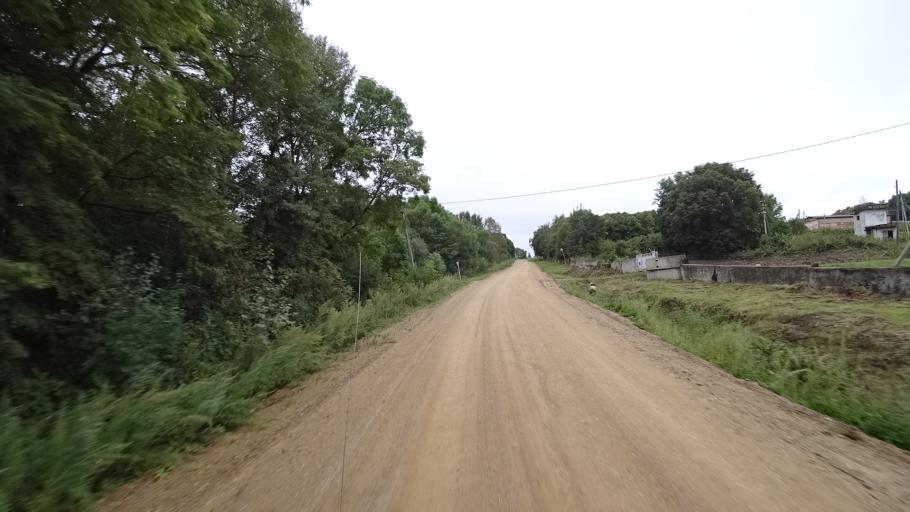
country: RU
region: Primorskiy
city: Rettikhovka
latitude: 44.1783
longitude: 132.8522
